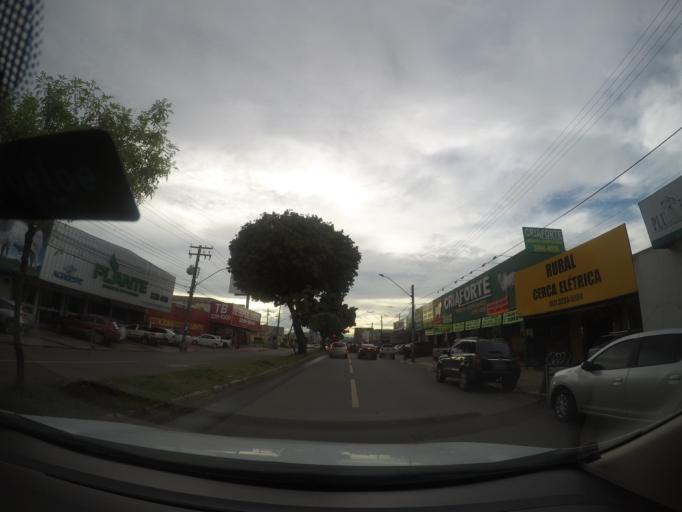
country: BR
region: Goias
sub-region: Goiania
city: Goiania
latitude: -16.6753
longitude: -49.2923
